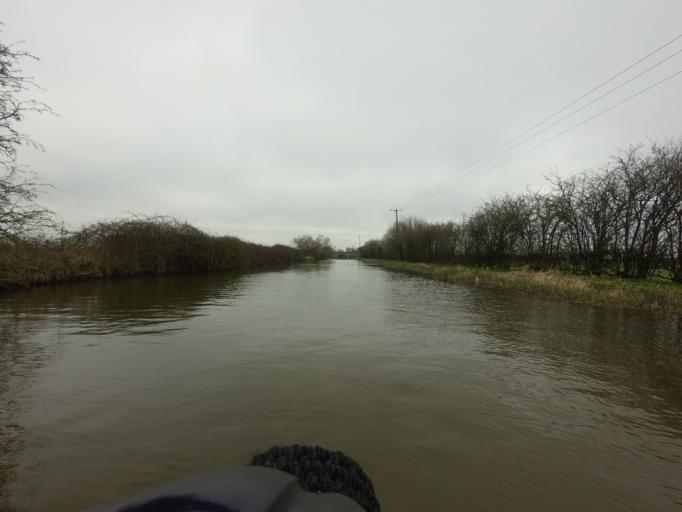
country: GB
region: England
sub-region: Buckinghamshire
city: Cheddington
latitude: 51.8686
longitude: -0.6486
